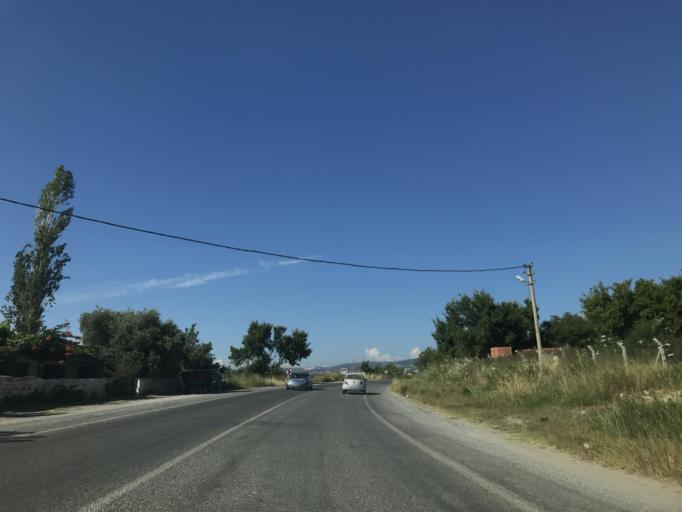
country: TR
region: Aydin
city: Davutlar
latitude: 37.7238
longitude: 27.2567
